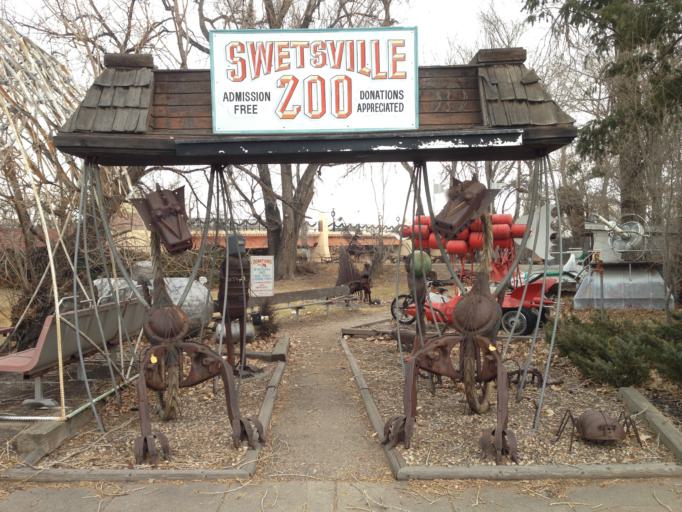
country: US
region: Colorado
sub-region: Weld County
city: Windsor
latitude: 40.5225
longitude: -104.9874
